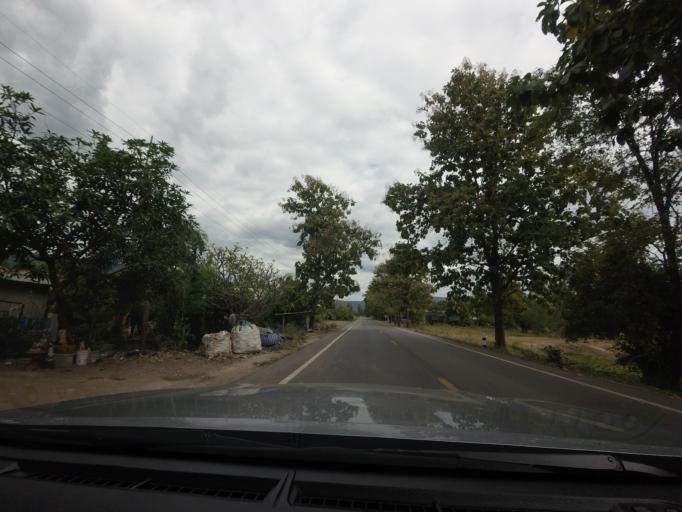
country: TH
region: Phitsanulok
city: Noen Maprang
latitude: 16.6946
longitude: 100.5544
